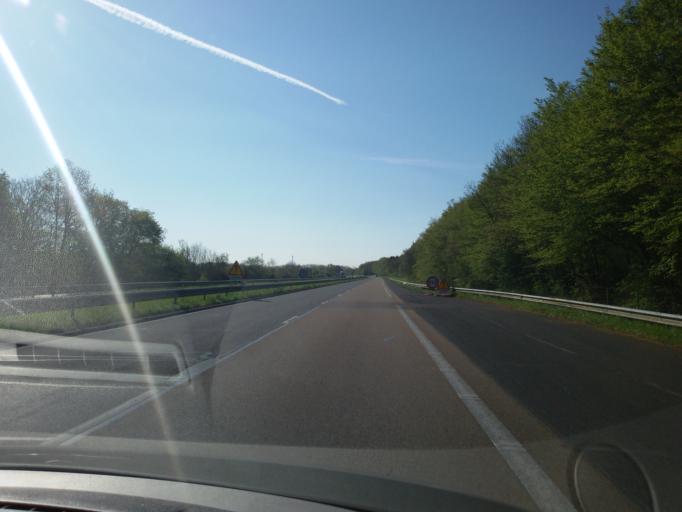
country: FR
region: Bourgogne
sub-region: Departement de l'Yonne
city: Cheroy
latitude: 48.1235
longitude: 2.9704
